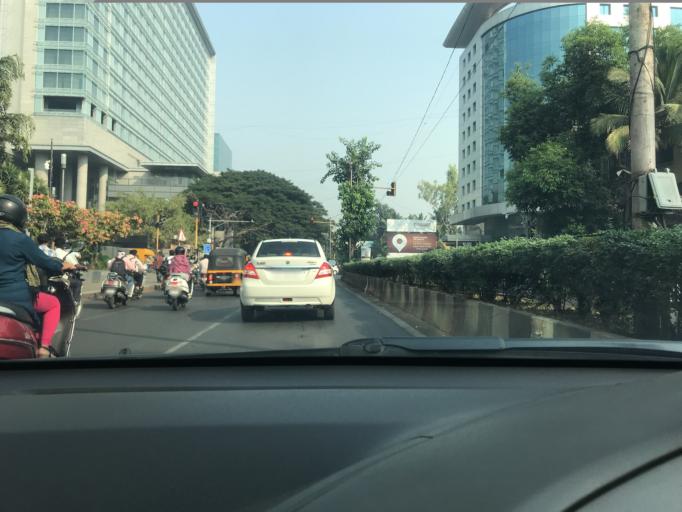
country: IN
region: Maharashtra
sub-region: Pune Division
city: Shivaji Nagar
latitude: 18.5311
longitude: 73.8300
